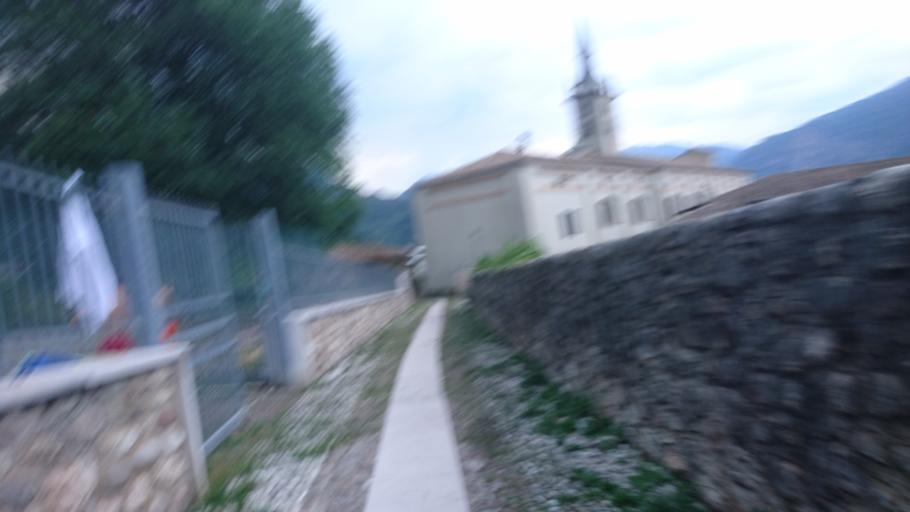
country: IT
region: Trentino-Alto Adige
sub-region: Provincia di Trento
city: Villa Lagarina
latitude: 45.9171
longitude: 11.0296
